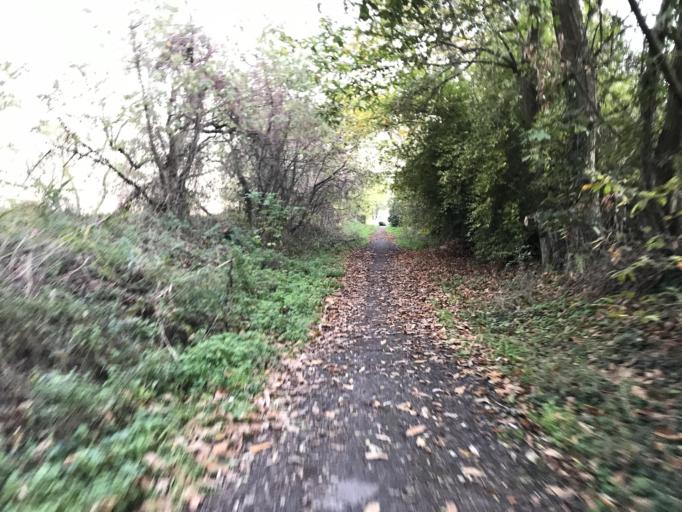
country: FR
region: Ile-de-France
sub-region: Departement de l'Essonne
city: Saulx-les-Chartreux
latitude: 48.6773
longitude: 2.2771
